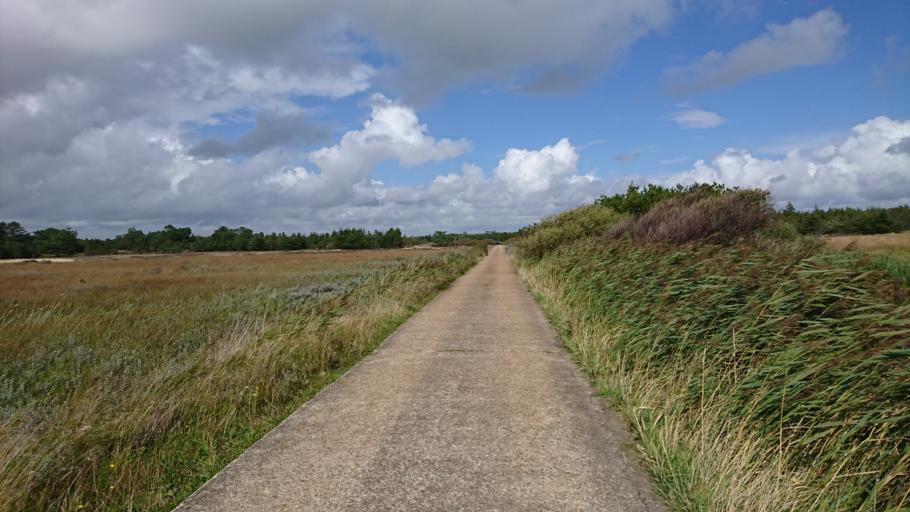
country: DK
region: South Denmark
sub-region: Fano Kommune
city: Nordby
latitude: 55.3860
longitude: 8.4169
